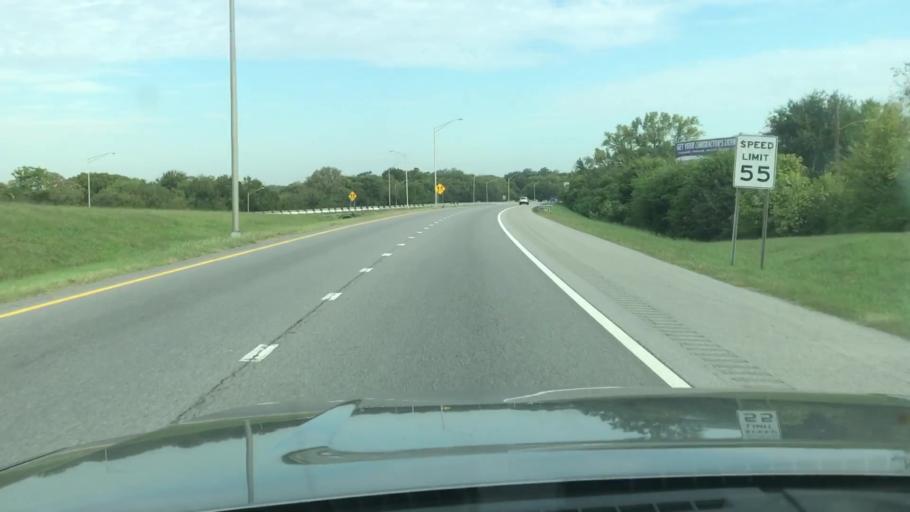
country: US
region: Tennessee
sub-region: Davidson County
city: Nashville
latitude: 36.1738
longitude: -86.7999
